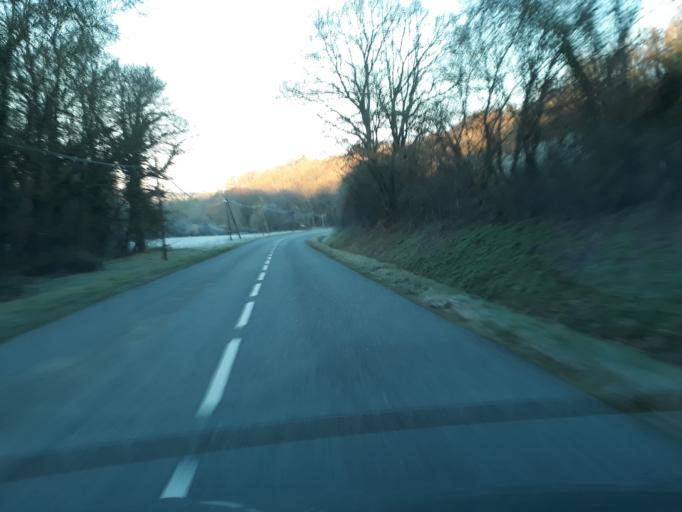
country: FR
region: Midi-Pyrenees
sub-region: Departement du Gers
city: Pavie
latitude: 43.6197
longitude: 0.6663
